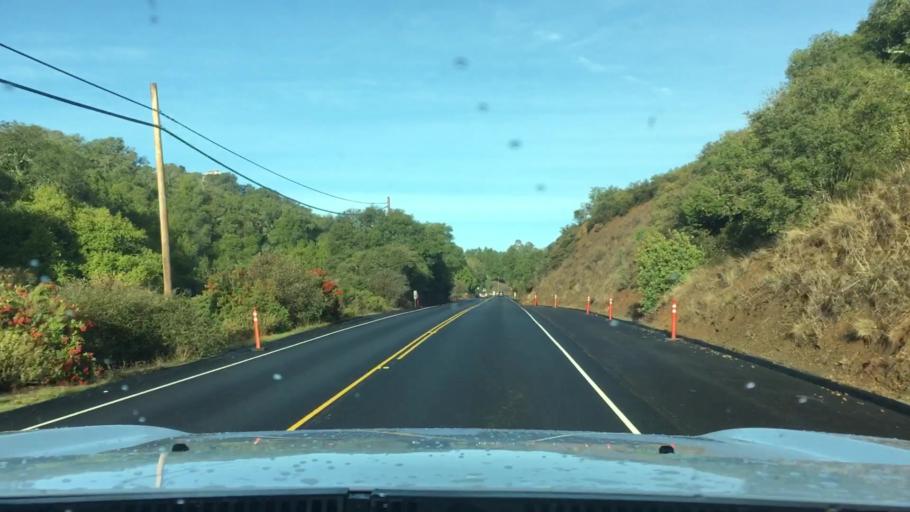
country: US
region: California
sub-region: San Luis Obispo County
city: Atascadero
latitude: 35.4529
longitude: -120.7104
